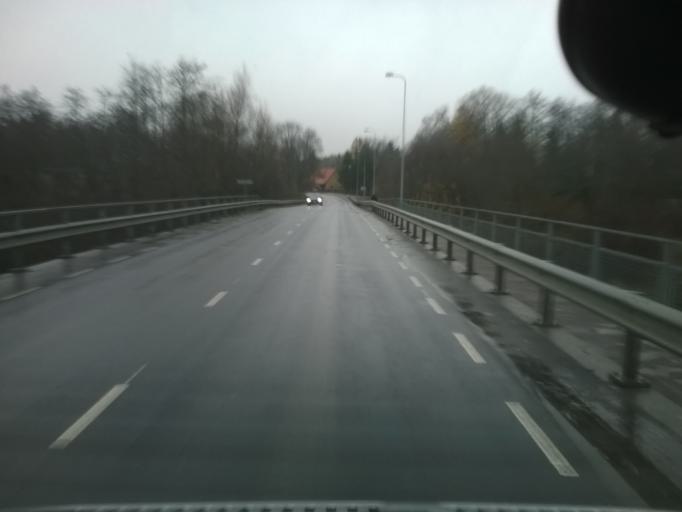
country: EE
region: Harju
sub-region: Saku vald
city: Saku
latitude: 59.2338
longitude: 24.6821
